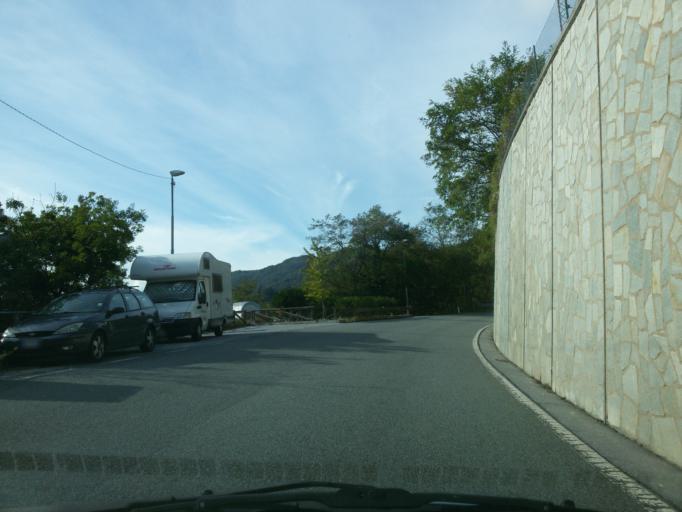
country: IT
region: Liguria
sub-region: Provincia di Genova
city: Piccarello
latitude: 44.4875
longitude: 8.9754
